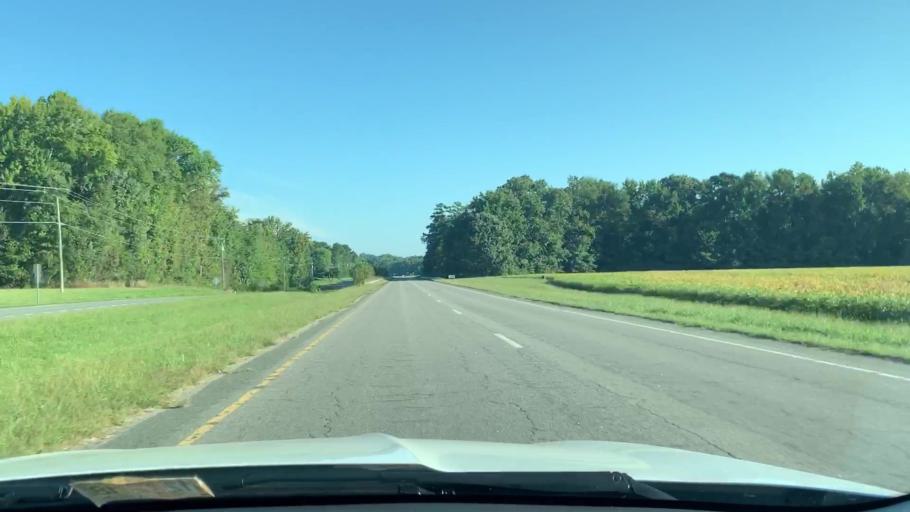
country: US
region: Virginia
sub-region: Lancaster County
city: Kilmarnock
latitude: 37.6884
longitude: -76.3761
